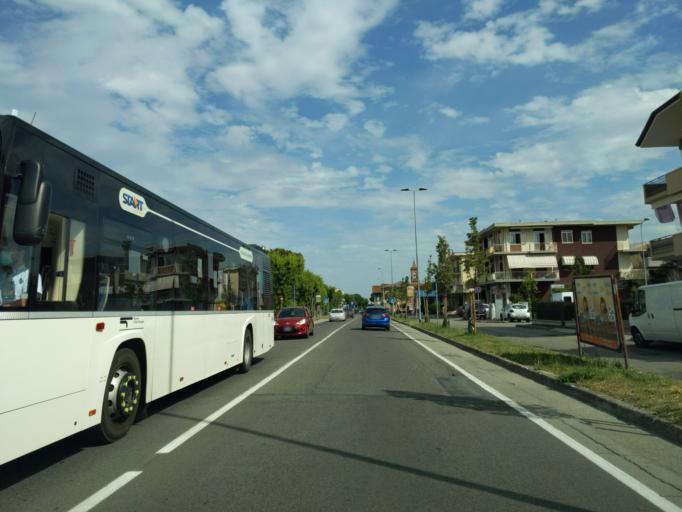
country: IT
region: Emilia-Romagna
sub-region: Provincia di Rimini
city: Rivazzurra
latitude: 44.0445
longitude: 12.5859
